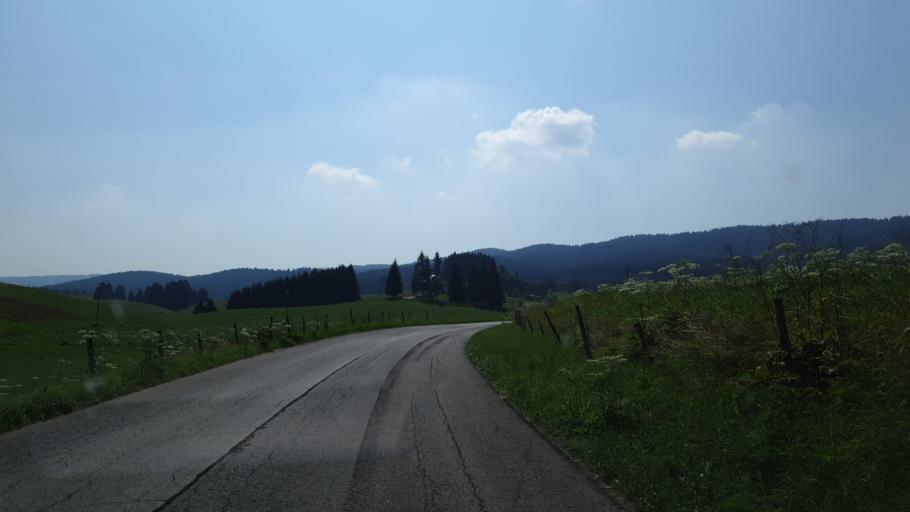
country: IT
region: Veneto
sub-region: Provincia di Vicenza
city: Asiago
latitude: 45.8596
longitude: 11.4980
